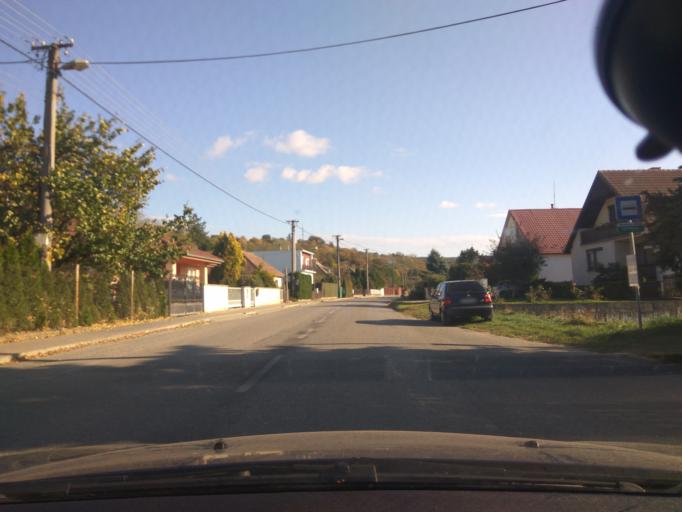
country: SK
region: Trnavsky
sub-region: Okres Trnava
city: Piestany
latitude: 48.5552
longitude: 17.8385
